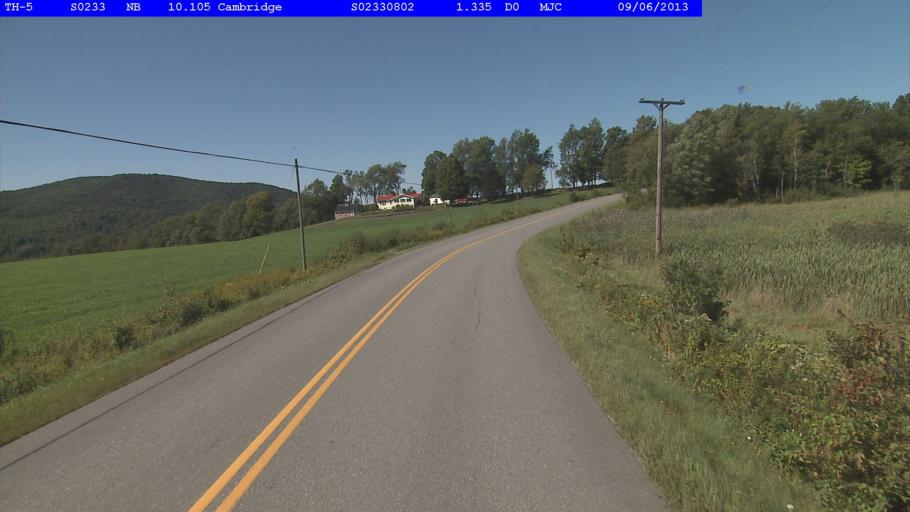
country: US
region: Vermont
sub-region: Chittenden County
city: Jericho
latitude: 44.6011
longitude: -72.8566
